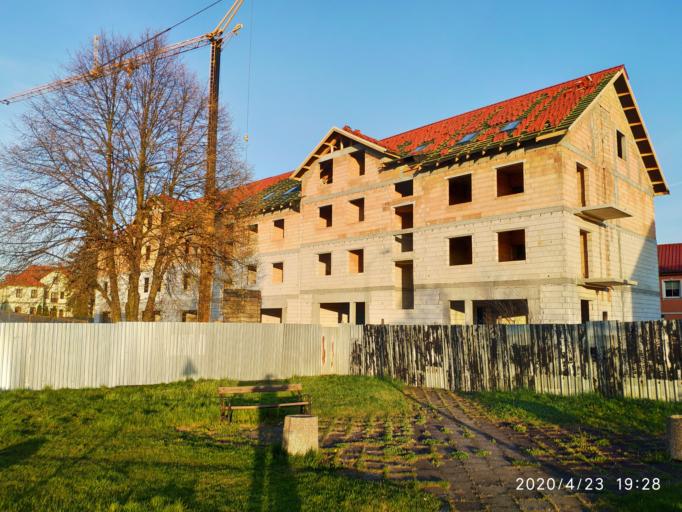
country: PL
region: Lesser Poland Voivodeship
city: Sulecin
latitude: 52.4434
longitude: 15.1113
